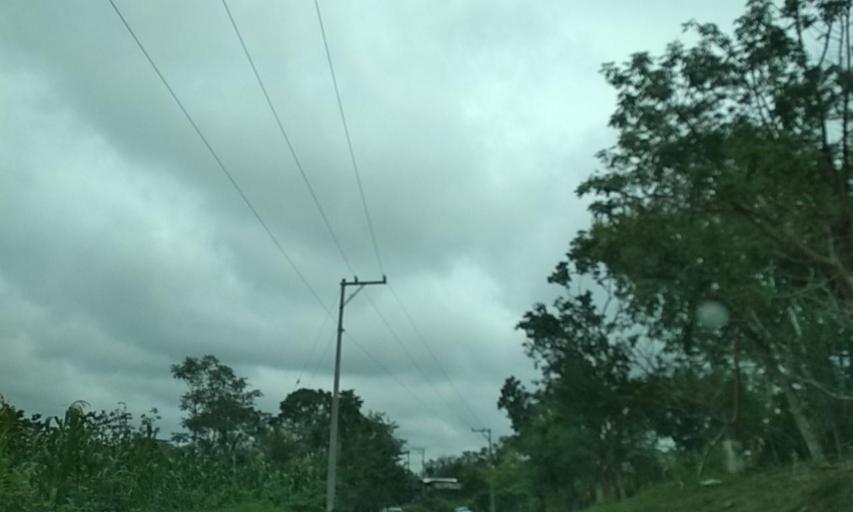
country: MX
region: Puebla
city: Espinal
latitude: 20.3164
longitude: -97.4159
